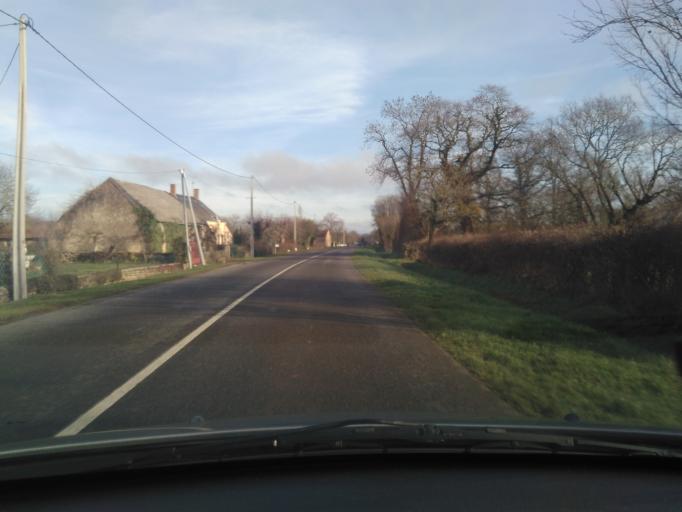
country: FR
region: Centre
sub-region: Departement de l'Indre
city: Montgivray
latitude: 46.6199
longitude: 2.0480
